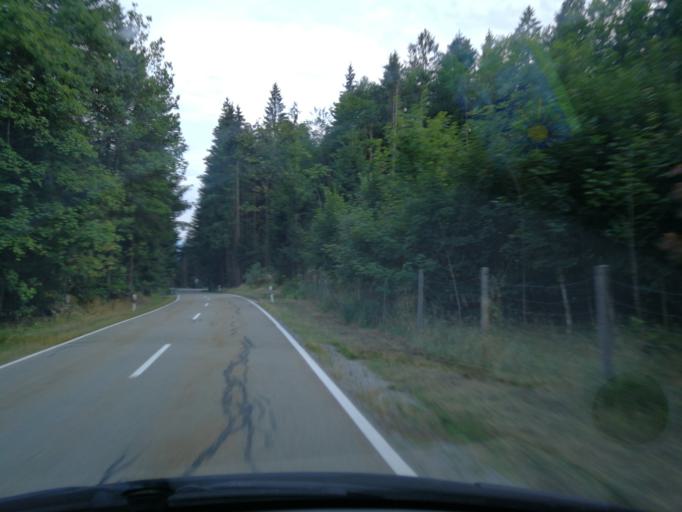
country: DE
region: Bavaria
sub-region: Lower Bavaria
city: Haibach
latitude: 49.0357
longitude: 12.7509
